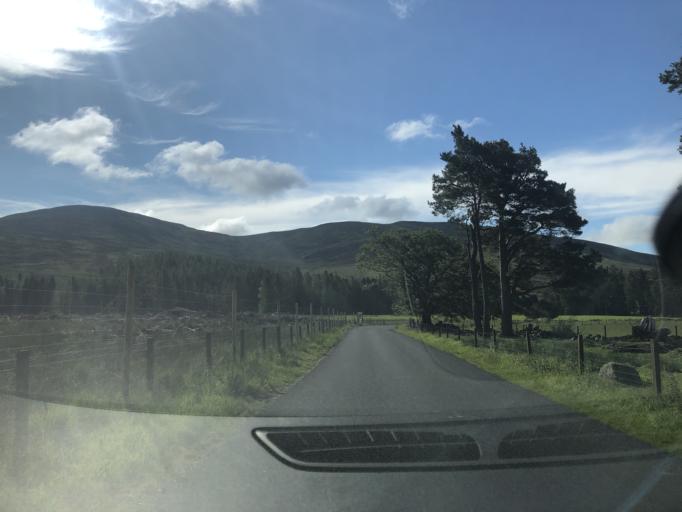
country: GB
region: Scotland
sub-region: Angus
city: Kirriemuir
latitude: 56.8178
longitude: -3.0342
